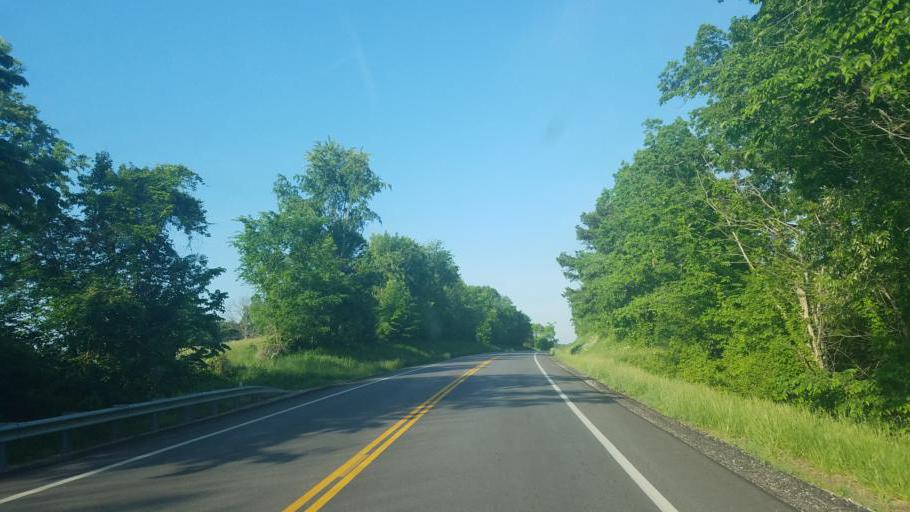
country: US
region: West Virginia
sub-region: Mason County
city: New Haven
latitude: 39.0696
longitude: -81.9364
